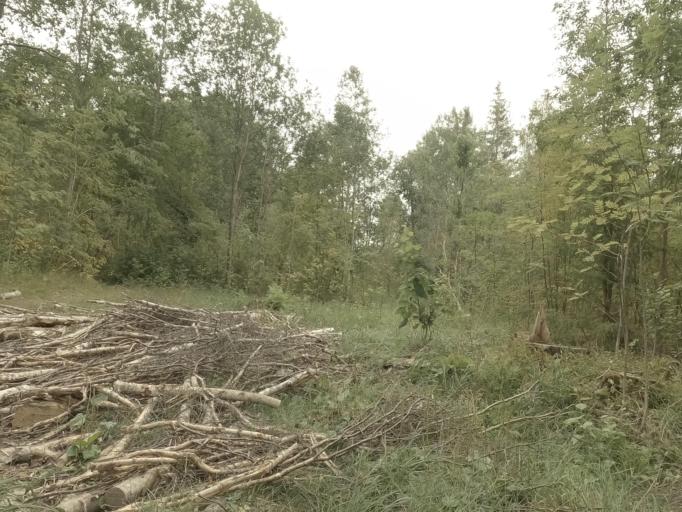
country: RU
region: Leningrad
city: Kamennogorsk
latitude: 61.0741
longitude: 29.1580
